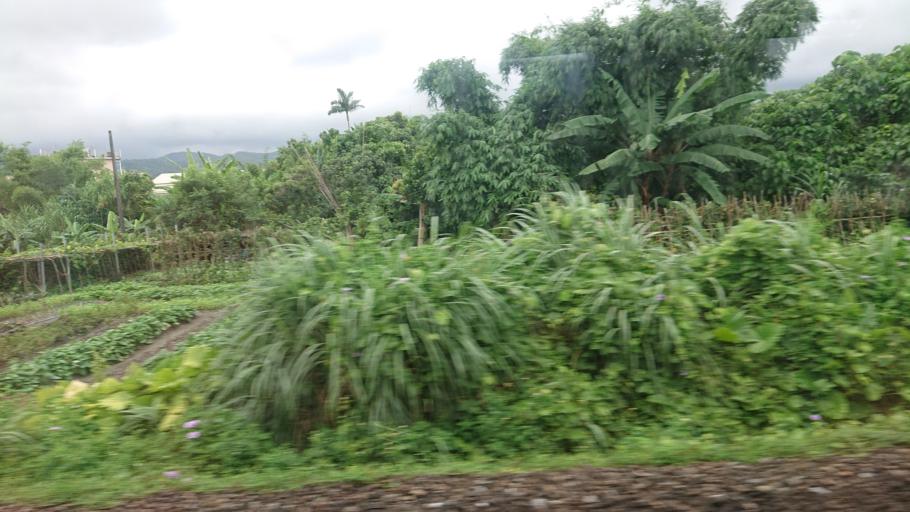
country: TW
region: Taiwan
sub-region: Yilan
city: Yilan
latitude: 24.8135
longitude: 121.7695
